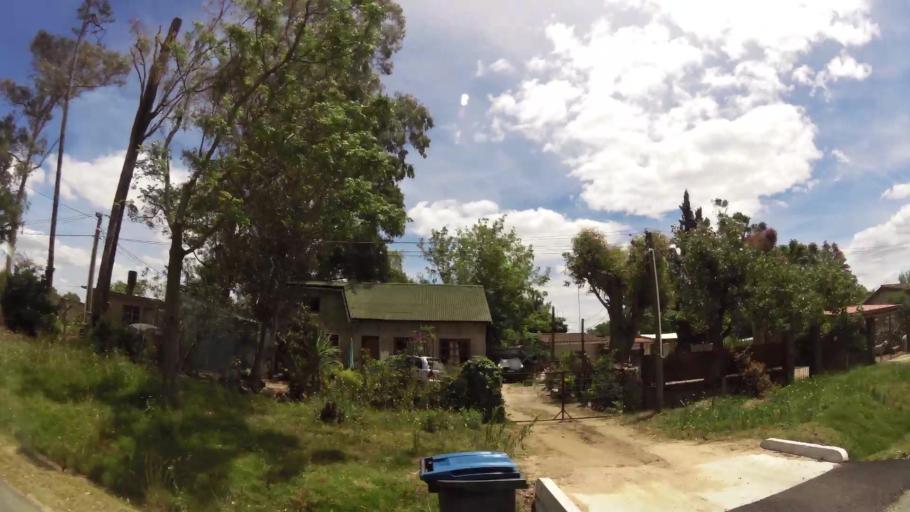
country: UY
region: Canelones
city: Colonia Nicolich
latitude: -34.8231
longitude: -55.9708
